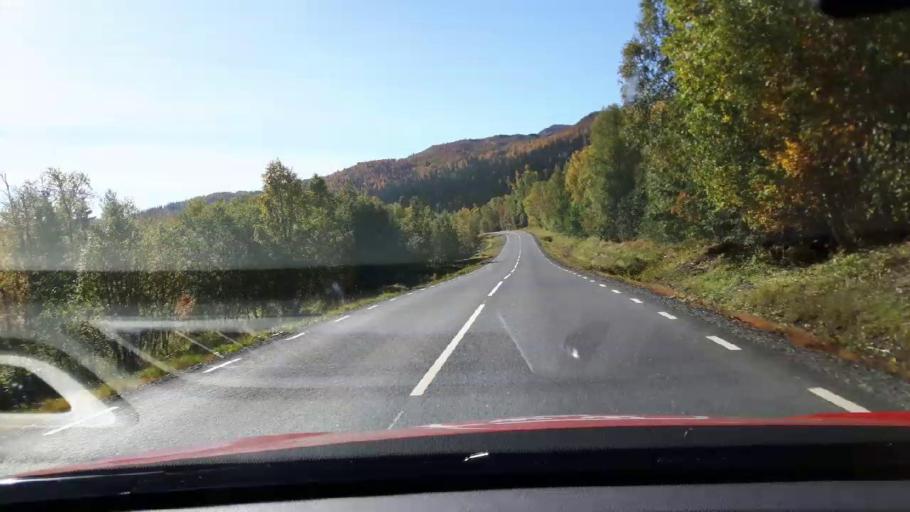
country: NO
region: Nord-Trondelag
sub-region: Royrvik
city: Royrvik
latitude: 64.8710
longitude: 14.2028
